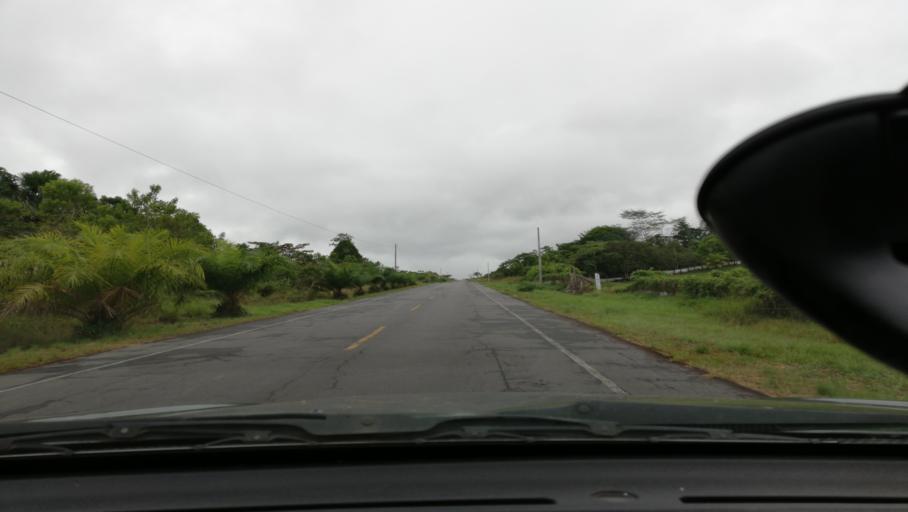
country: PE
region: Loreto
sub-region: Provincia de Loreto
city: Nauta
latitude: -4.3501
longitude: -73.5450
